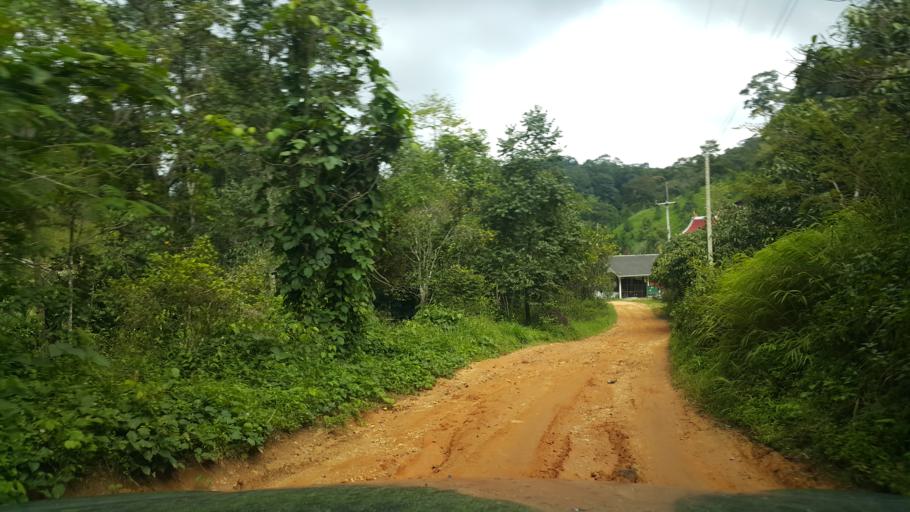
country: TH
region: Lampang
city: Wang Nuea
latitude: 19.1160
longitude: 99.3648
